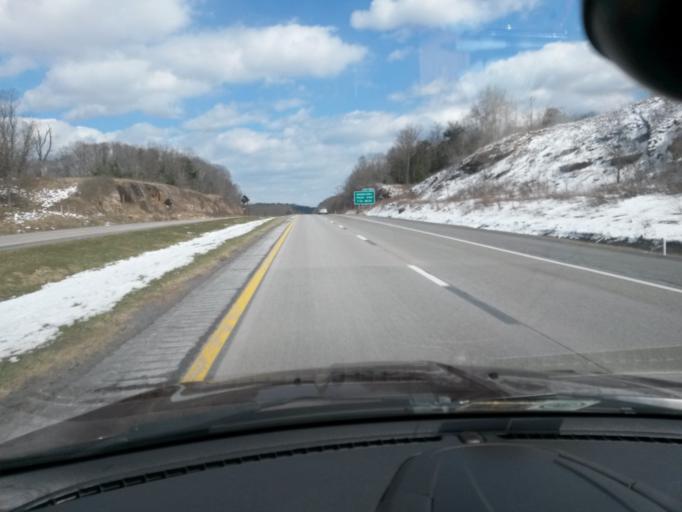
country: US
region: West Virginia
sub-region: Raleigh County
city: Shady Spring
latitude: 37.7658
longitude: -81.0230
